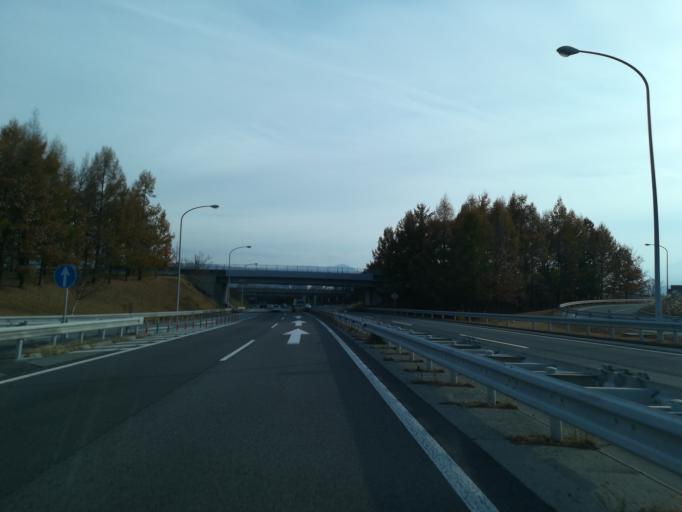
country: JP
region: Nagano
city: Komoro
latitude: 36.2882
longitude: 138.4833
